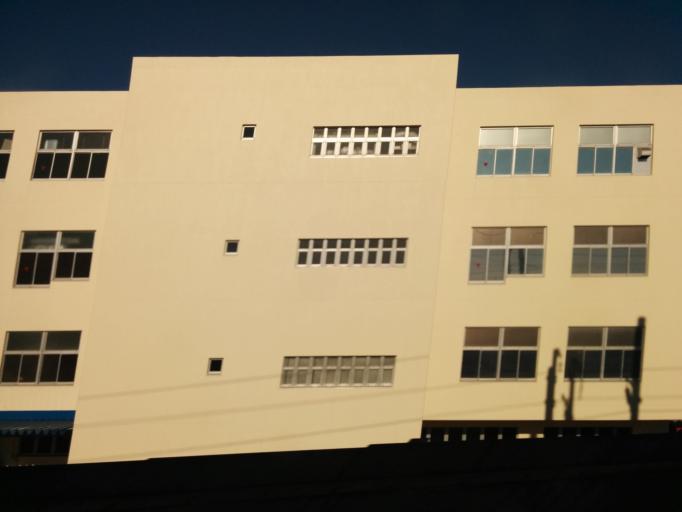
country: JP
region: Kanagawa
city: Odawara
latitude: 35.2742
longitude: 139.1729
